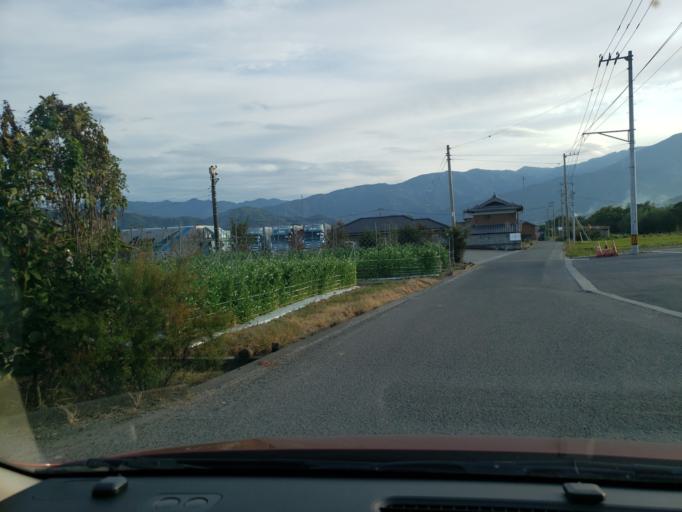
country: JP
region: Tokushima
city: Wakimachi
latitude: 34.0799
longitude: 134.2285
